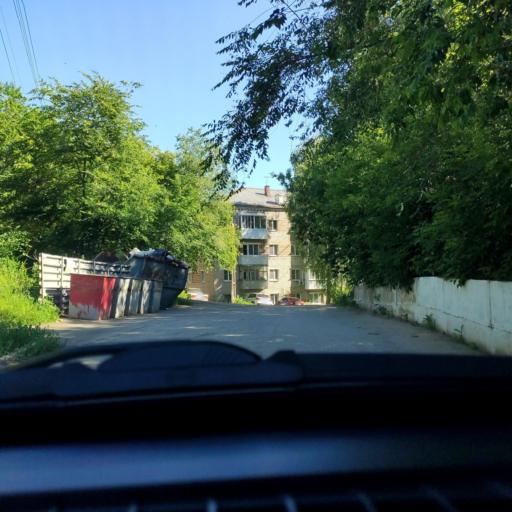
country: RU
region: Samara
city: Zhigulevsk
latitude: 53.4075
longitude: 49.4722
